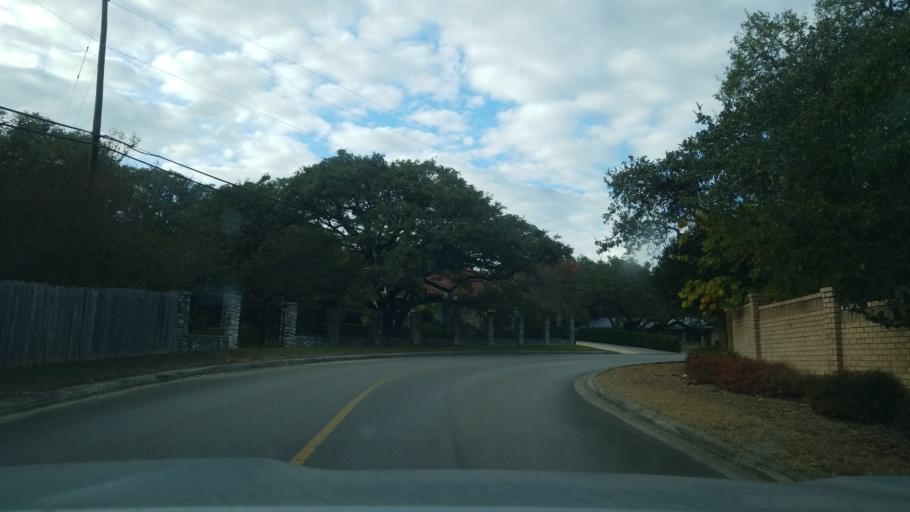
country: US
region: Texas
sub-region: Bexar County
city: Hollywood Park
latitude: 29.6003
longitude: -98.4815
